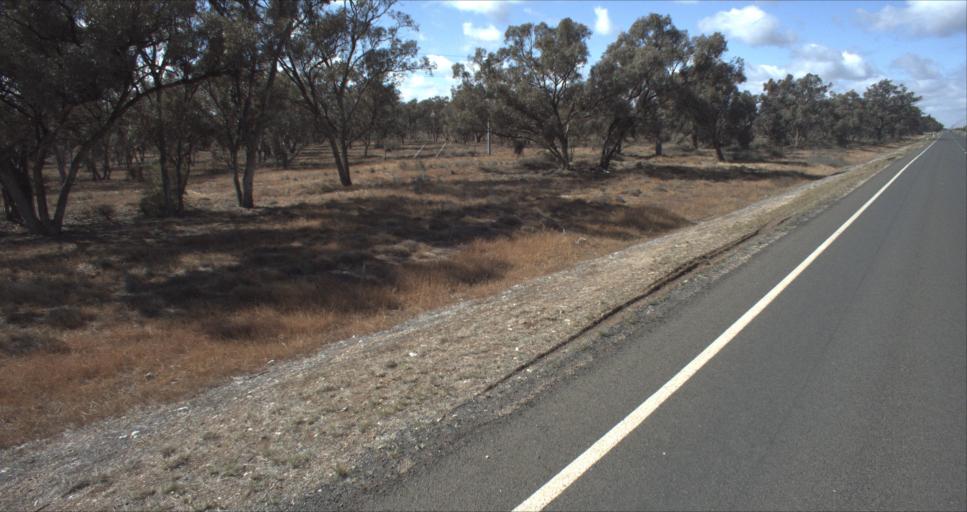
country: AU
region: New South Wales
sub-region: Murrumbidgee Shire
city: Darlington Point
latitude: -34.5209
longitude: 146.1757
